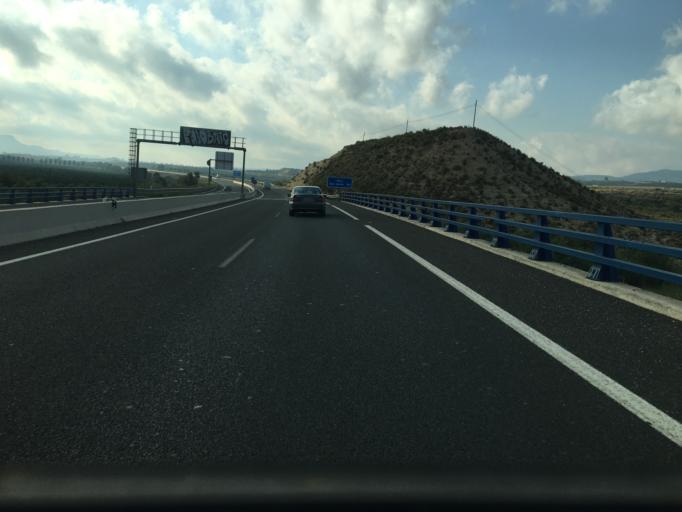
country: ES
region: Murcia
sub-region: Murcia
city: Beniel
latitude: 37.9972
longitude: -1.0060
